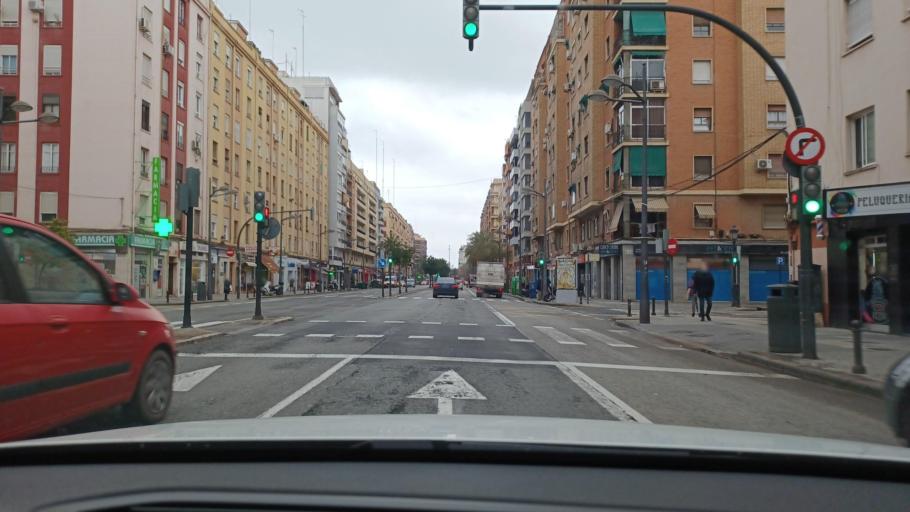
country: ES
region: Valencia
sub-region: Provincia de Valencia
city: Valencia
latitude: 39.4724
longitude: -0.3538
